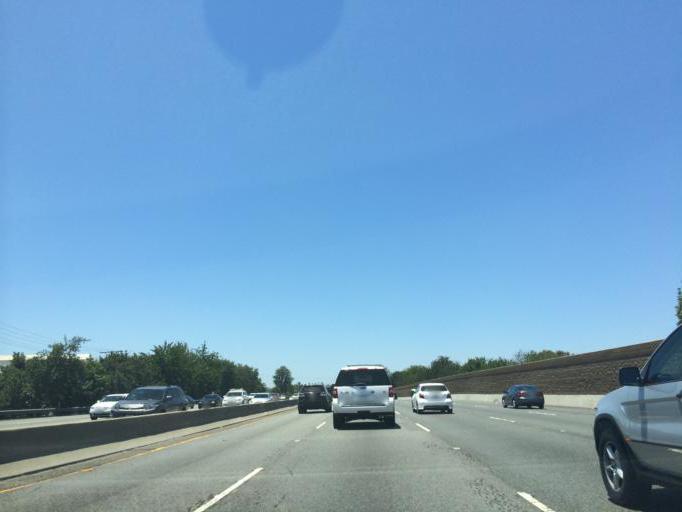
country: US
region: California
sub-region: Los Angeles County
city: Woodland Hills
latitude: 34.1737
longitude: -118.5592
